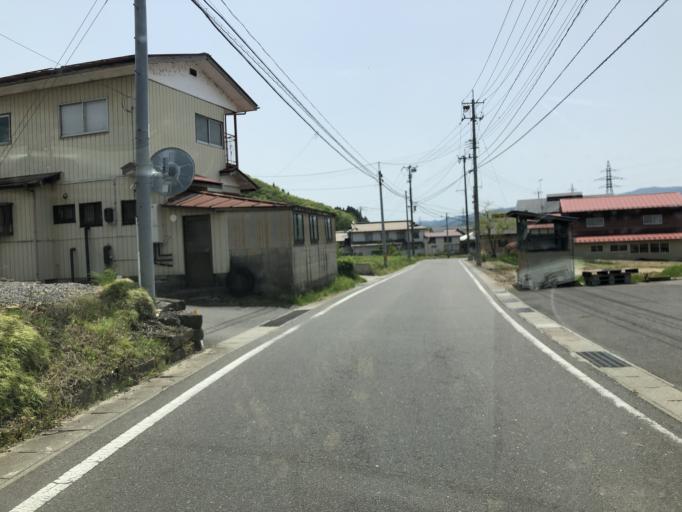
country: JP
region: Fukushima
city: Ishikawa
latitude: 37.0277
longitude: 140.3939
